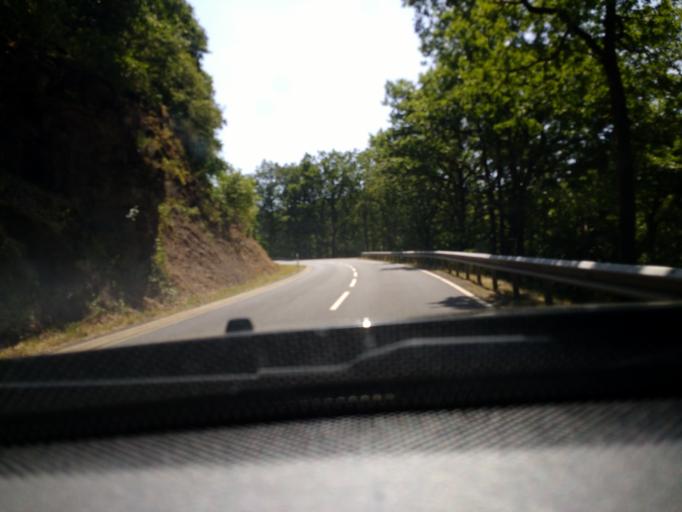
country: DE
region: Rheinland-Pfalz
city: Manderscheid
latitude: 50.0942
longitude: 6.7931
